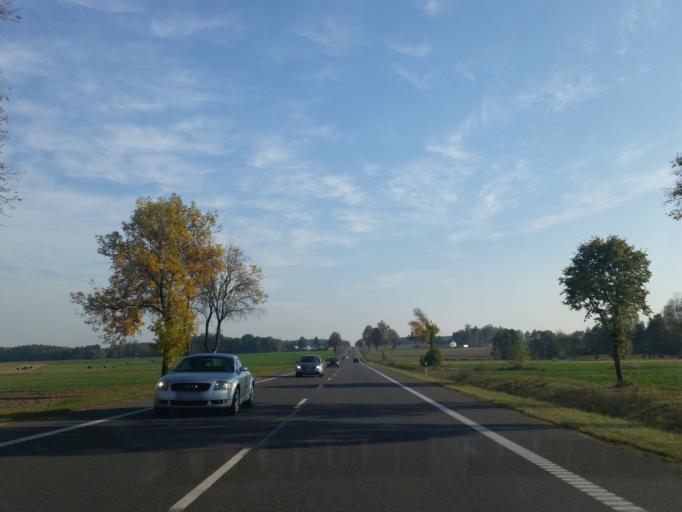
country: PL
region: Masovian Voivodeship
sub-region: Powiat plocki
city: Starozreby
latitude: 52.6801
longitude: 20.0605
